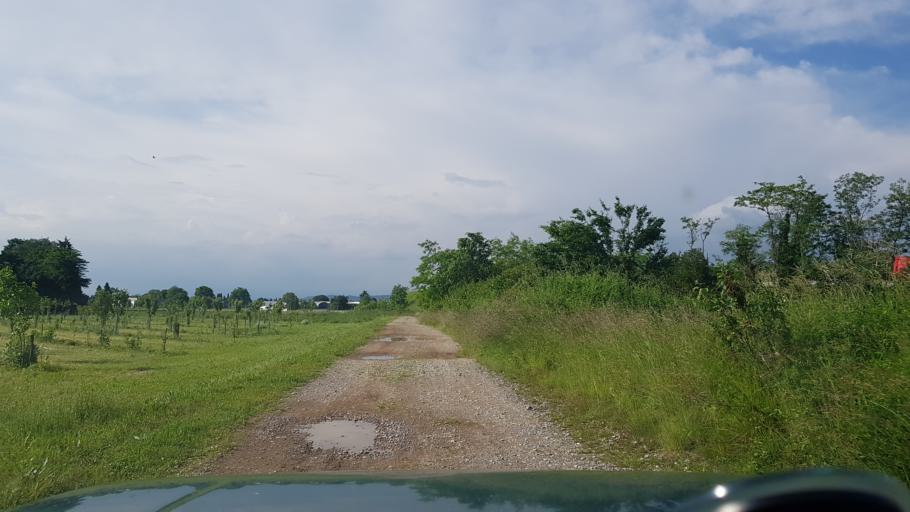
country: IT
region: Friuli Venezia Giulia
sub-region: Provincia di Gorizia
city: Mariano del Friuli
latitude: 45.9009
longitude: 13.4664
